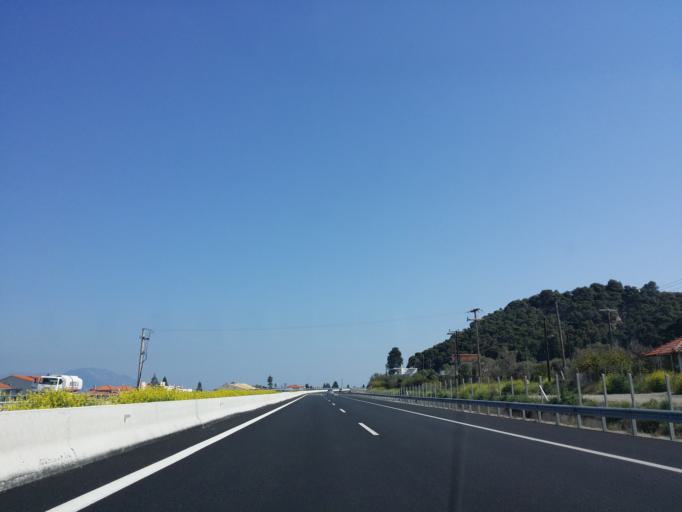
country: GR
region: Peloponnese
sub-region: Nomos Korinthias
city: Kato Dhiminio
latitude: 38.0422
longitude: 22.7031
